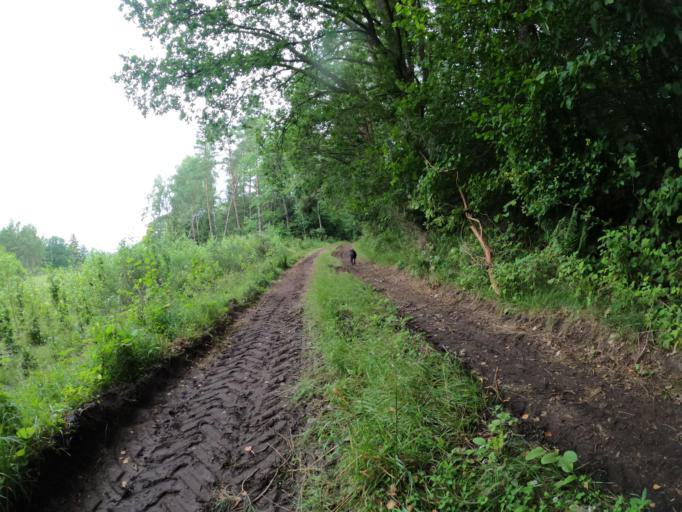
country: PL
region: West Pomeranian Voivodeship
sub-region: Powiat szczecinecki
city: Grzmiaca
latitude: 53.9729
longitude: 16.4383
